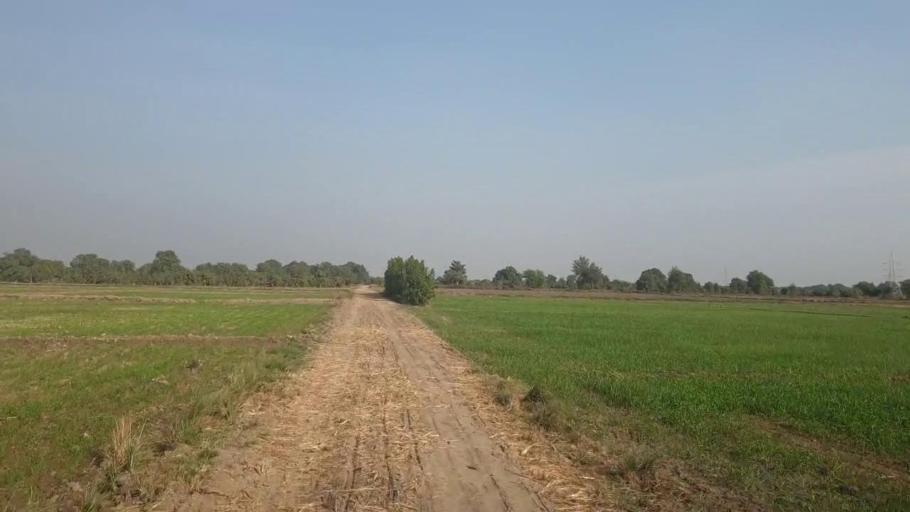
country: PK
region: Sindh
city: Tando Jam
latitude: 25.4296
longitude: 68.4761
